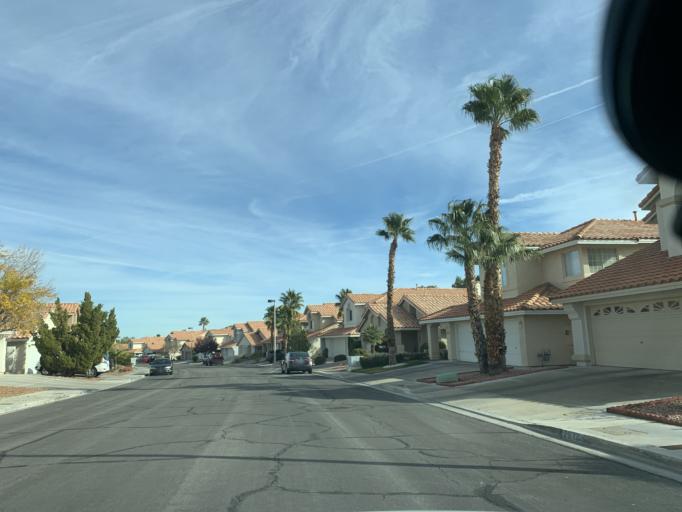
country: US
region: Nevada
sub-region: Clark County
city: Summerlin South
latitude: 36.1475
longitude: -115.3053
